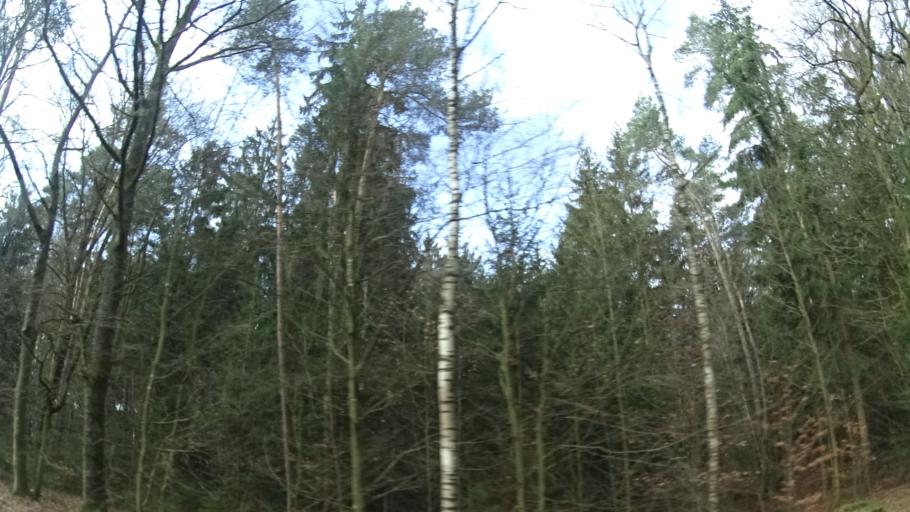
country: DE
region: Bavaria
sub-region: Regierungsbezirk Mittelfranken
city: Altdorf
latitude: 49.4058
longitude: 11.3444
